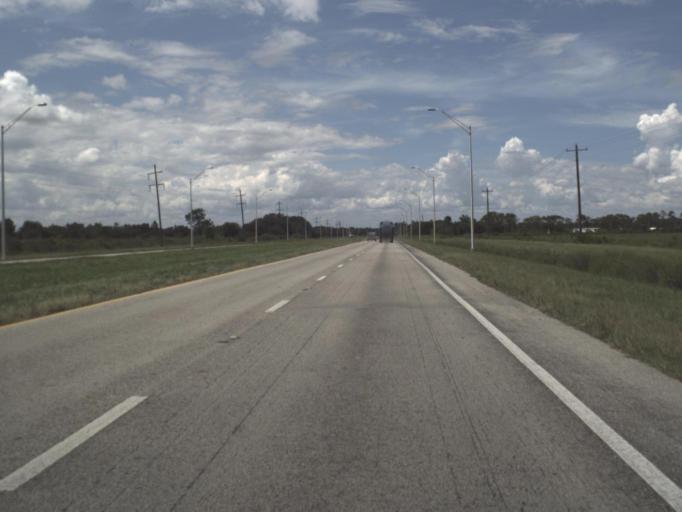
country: US
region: Florida
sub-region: Polk County
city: Babson Park
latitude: 27.8610
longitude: -81.3770
